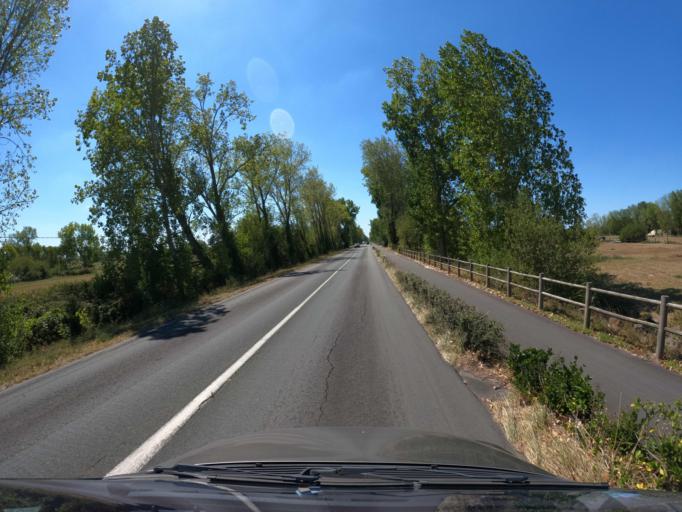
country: FR
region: Pays de la Loire
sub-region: Departement de la Vendee
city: Le Perrier
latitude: 46.8162
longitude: -1.9998
